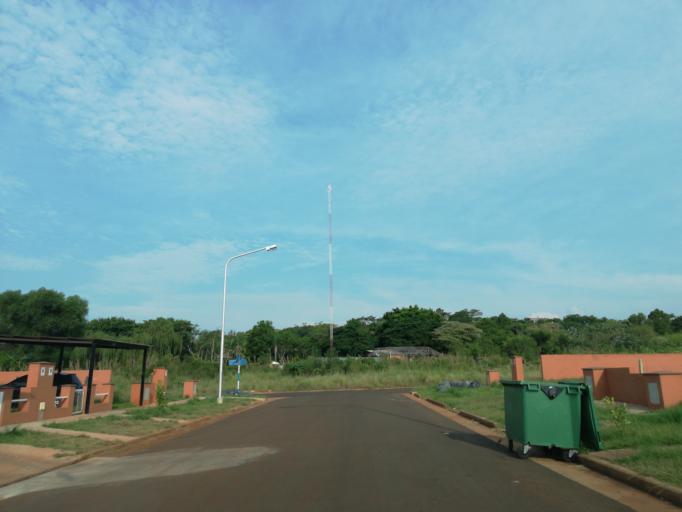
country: AR
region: Misiones
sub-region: Departamento de Capital
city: Posadas
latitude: -27.4055
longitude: -55.9793
